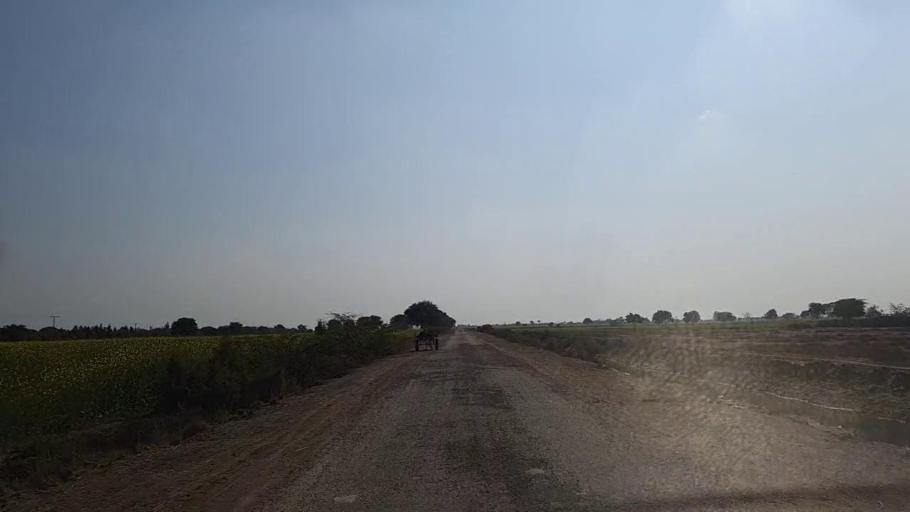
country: PK
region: Sindh
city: Jam Sahib
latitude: 26.2610
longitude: 68.5670
